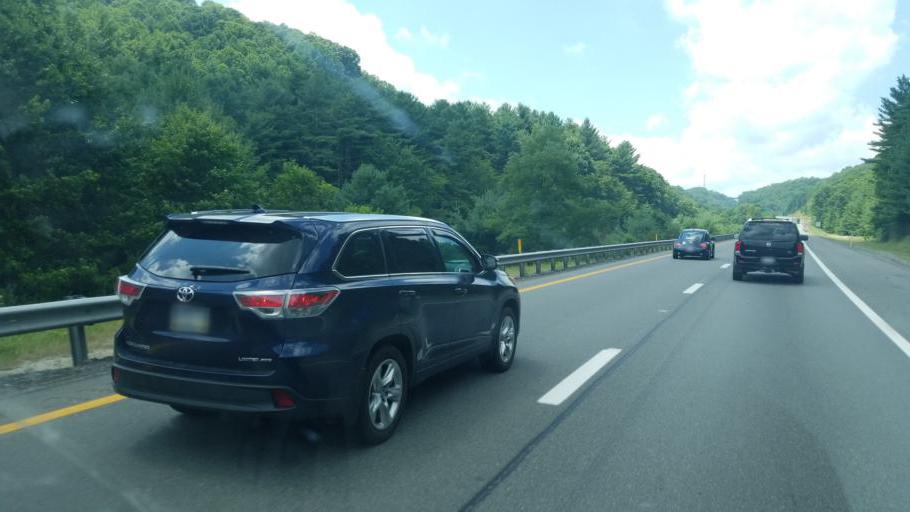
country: US
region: West Virginia
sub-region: Raleigh County
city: Beaver
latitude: 37.7186
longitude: -81.1633
